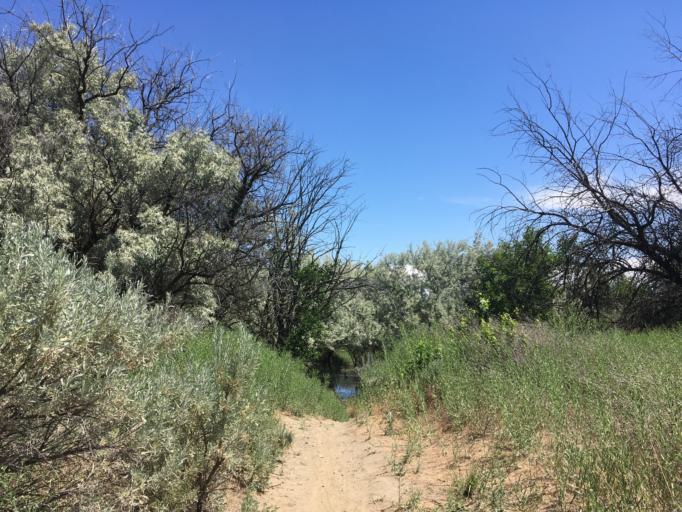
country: US
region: Washington
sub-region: Benton County
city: Richland
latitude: 46.2549
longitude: -119.2830
